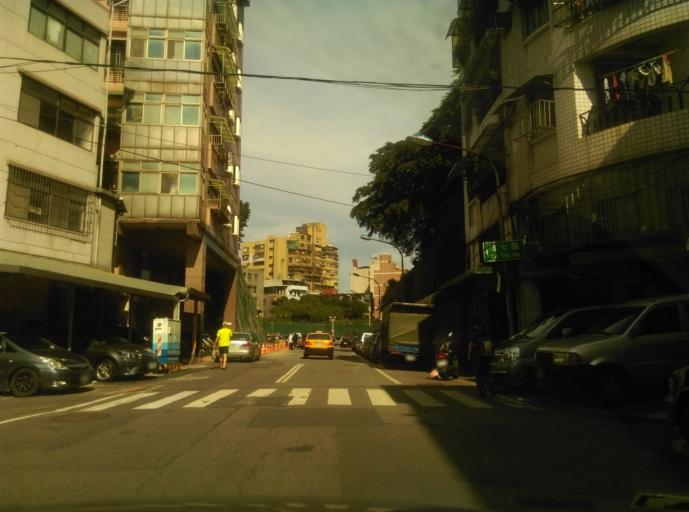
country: TW
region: Taiwan
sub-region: Keelung
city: Keelung
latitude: 25.1357
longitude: 121.7485
